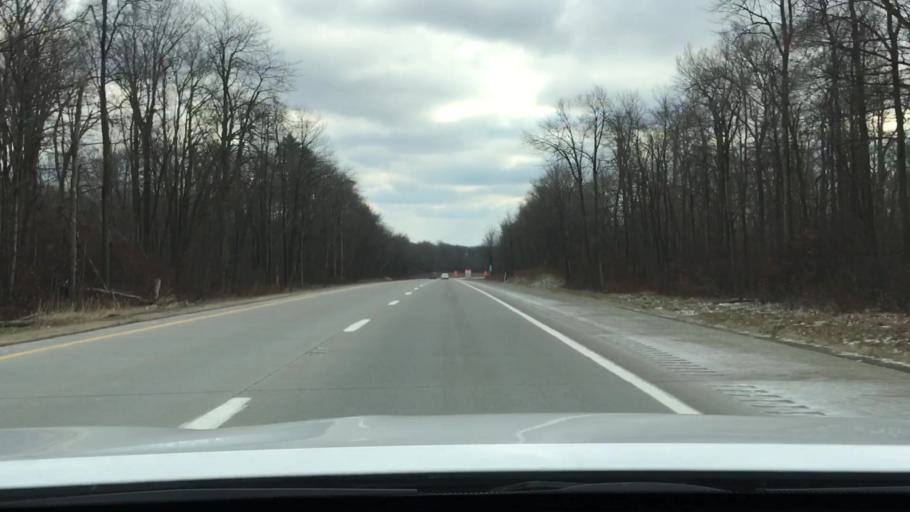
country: US
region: Pennsylvania
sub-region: Monroe County
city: Mount Pocono
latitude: 41.1474
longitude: -75.4066
